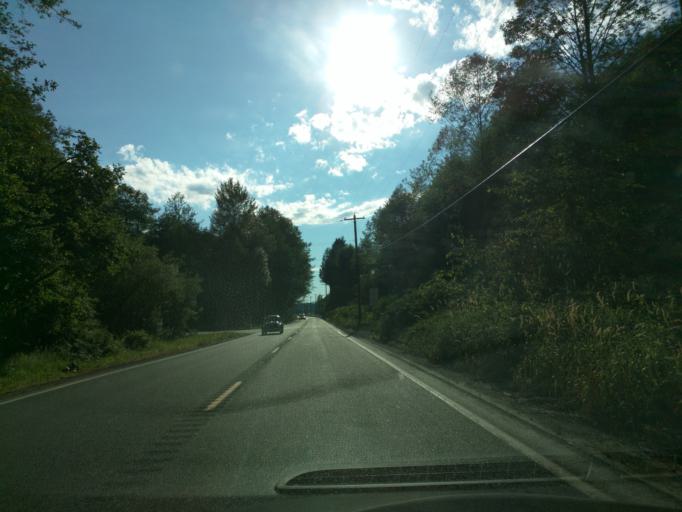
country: US
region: Washington
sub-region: Snohomish County
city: Darrington
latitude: 48.2772
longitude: -121.8202
